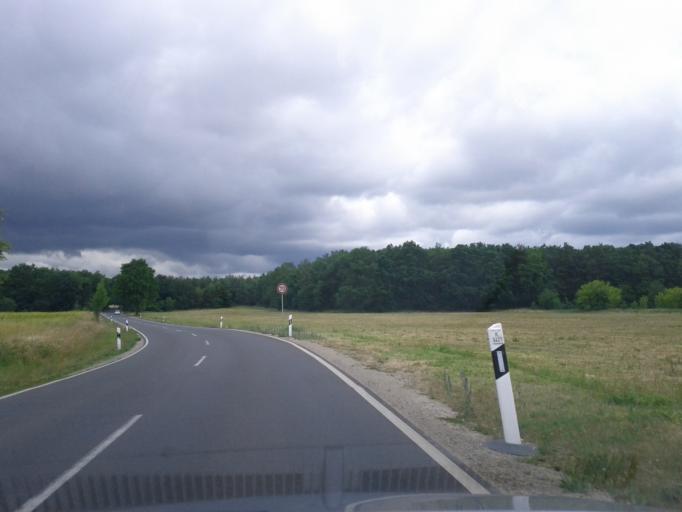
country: DE
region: Brandenburg
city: Woltersdorf
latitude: 52.4667
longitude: 13.7472
